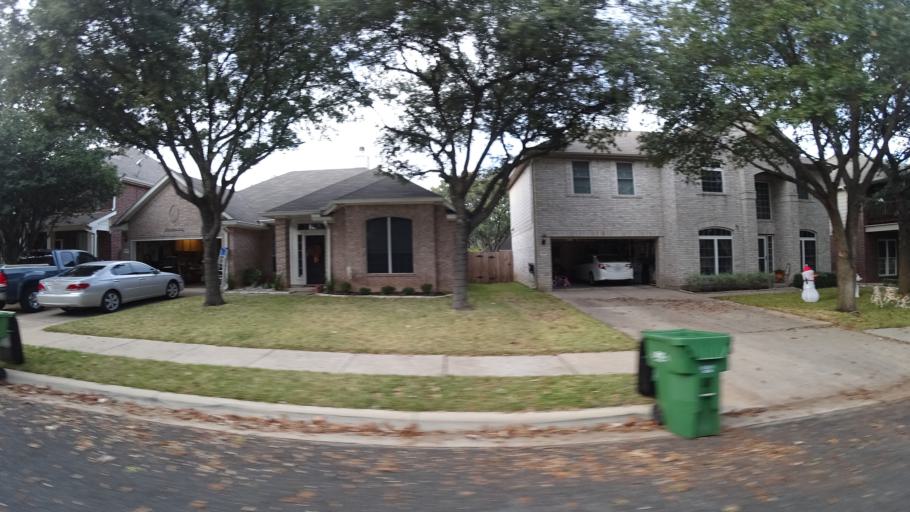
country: US
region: Texas
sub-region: Williamson County
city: Brushy Creek
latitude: 30.5133
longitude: -97.7223
